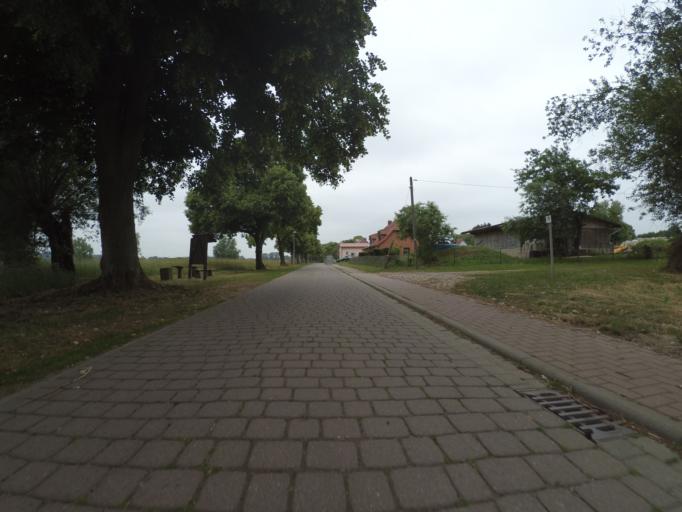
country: DE
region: Mecklenburg-Vorpommern
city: Goldberg
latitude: 53.5788
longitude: 12.0273
